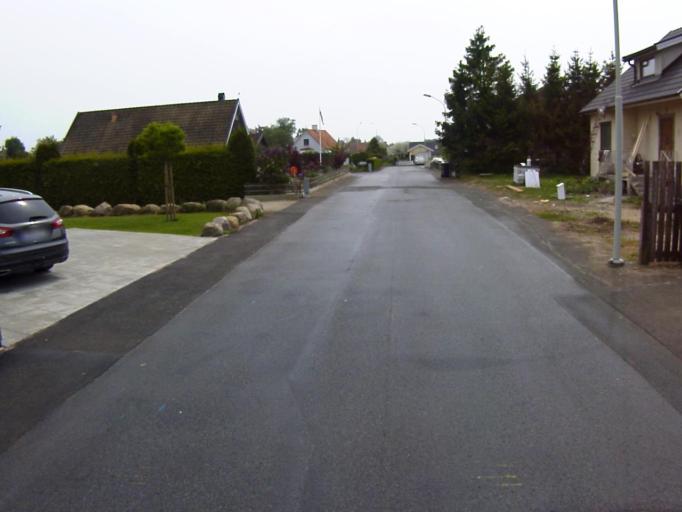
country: SE
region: Skane
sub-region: Kristianstads Kommun
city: Ahus
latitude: 55.9233
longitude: 14.2865
